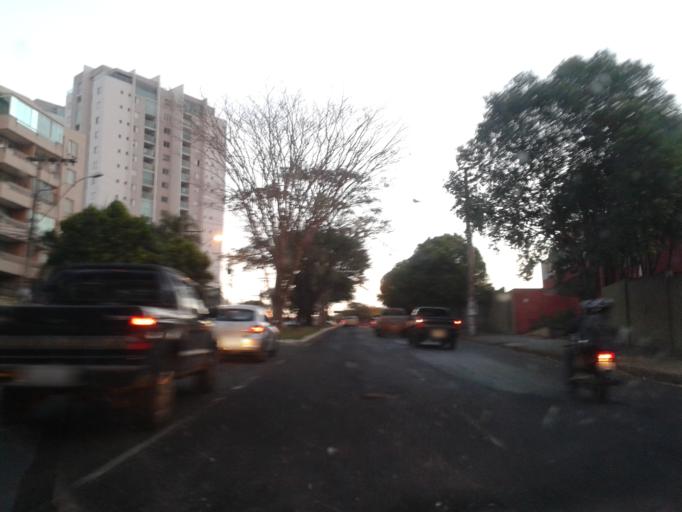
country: BR
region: Minas Gerais
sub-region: Uberlandia
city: Uberlandia
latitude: -18.9288
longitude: -48.2993
